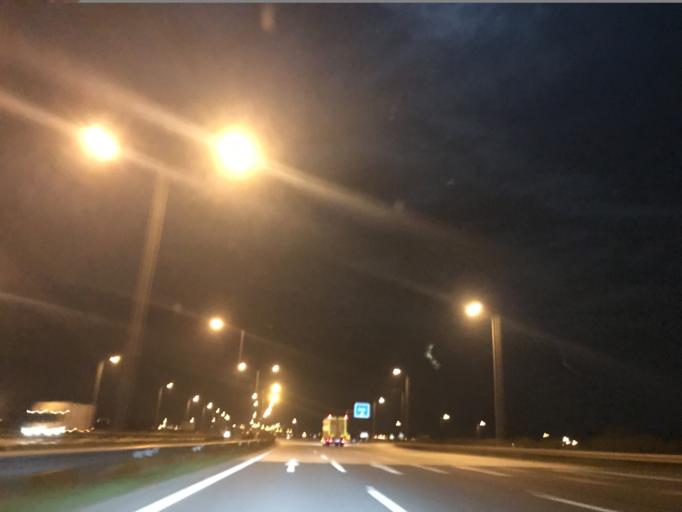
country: TR
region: Hatay
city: Mahmutlar
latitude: 36.9585
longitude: 36.1319
